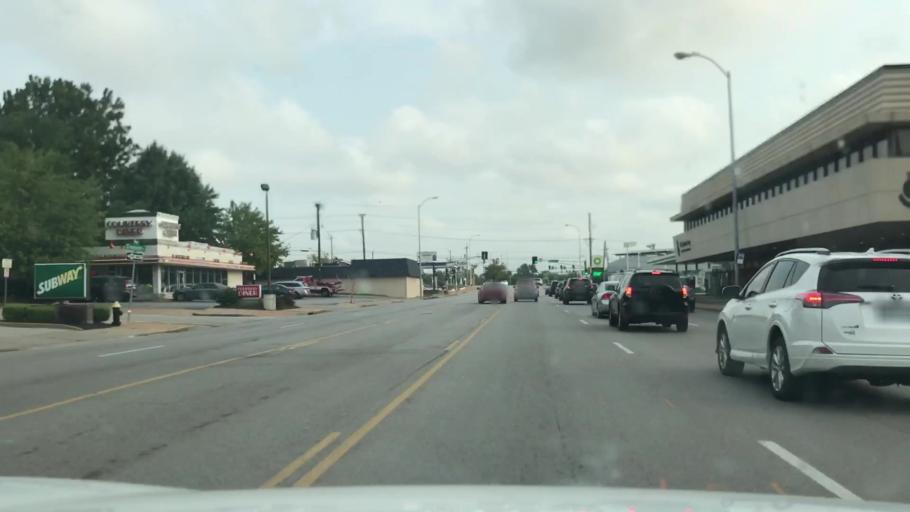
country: US
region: Missouri
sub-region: Saint Louis County
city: Richmond Heights
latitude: 38.6281
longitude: -90.2873
